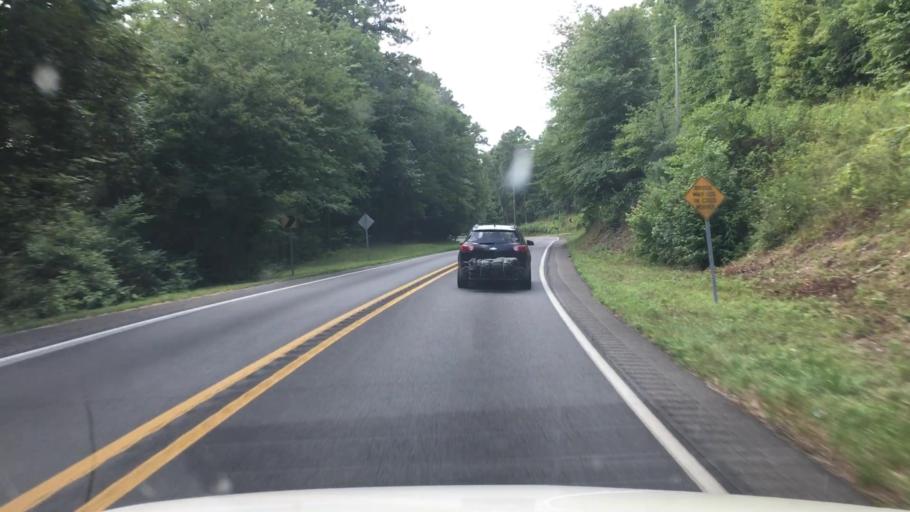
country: US
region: Arkansas
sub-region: Garland County
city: Lake Hamilton
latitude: 34.3432
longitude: -93.1838
